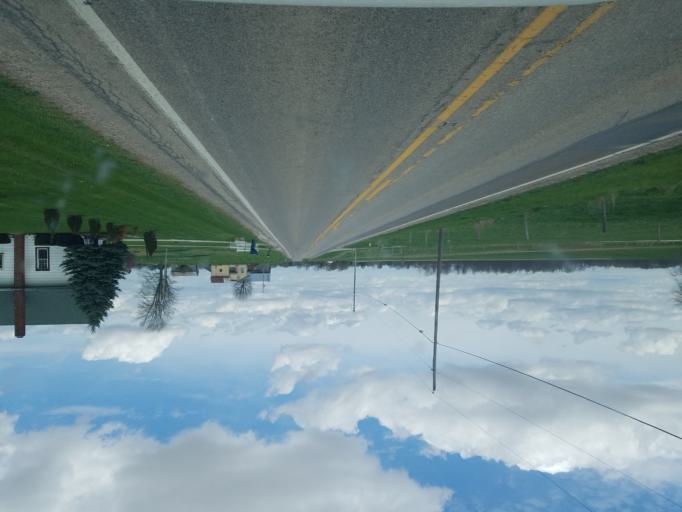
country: US
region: Ohio
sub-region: Crawford County
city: Bucyrus
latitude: 40.8478
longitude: -82.9911
